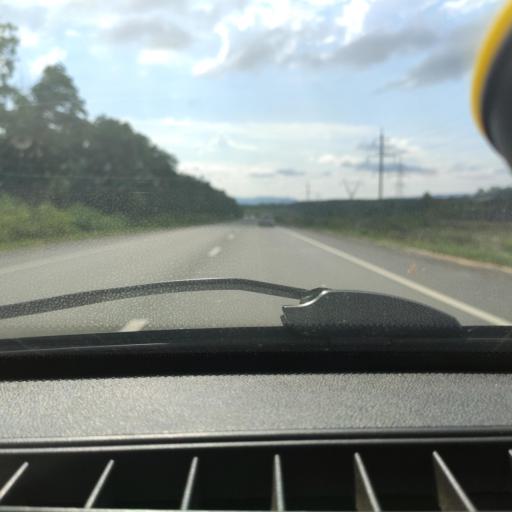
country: RU
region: Samara
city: Bogatyr'
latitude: 53.4987
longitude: 49.9561
